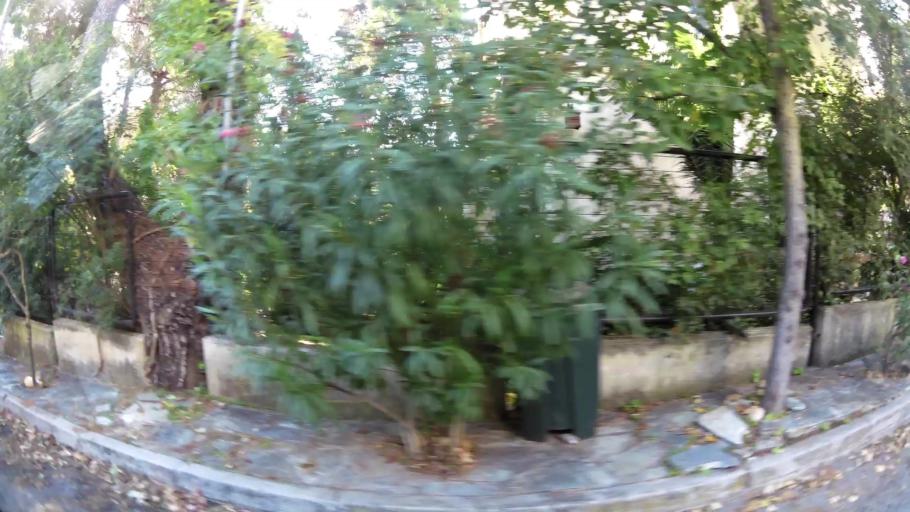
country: GR
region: Attica
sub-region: Nomarchia Athinas
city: Ekali
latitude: 38.1174
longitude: 23.8417
